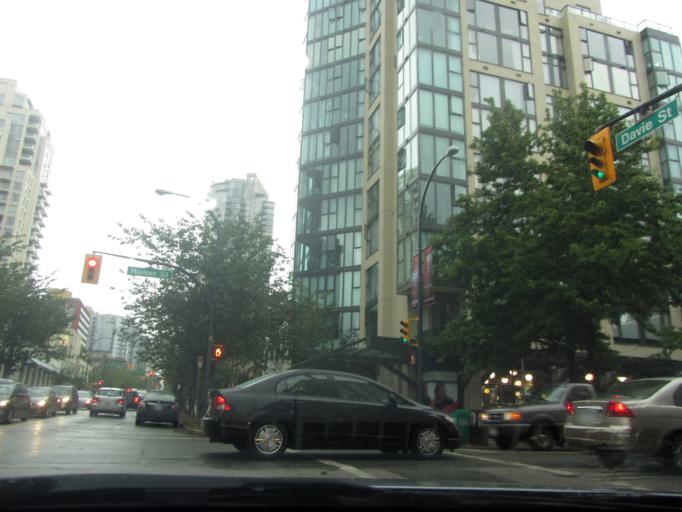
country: CA
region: British Columbia
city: West End
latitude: 49.2753
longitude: -123.1231
